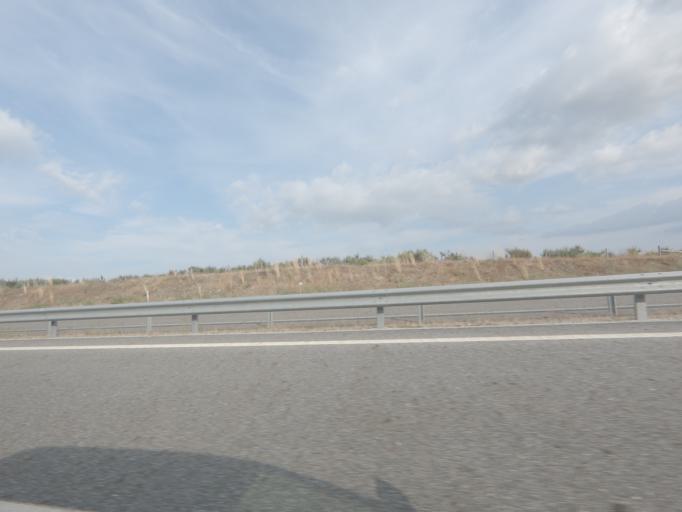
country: PT
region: Vila Real
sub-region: Chaves
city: Chaves
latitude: 41.7285
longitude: -7.5352
